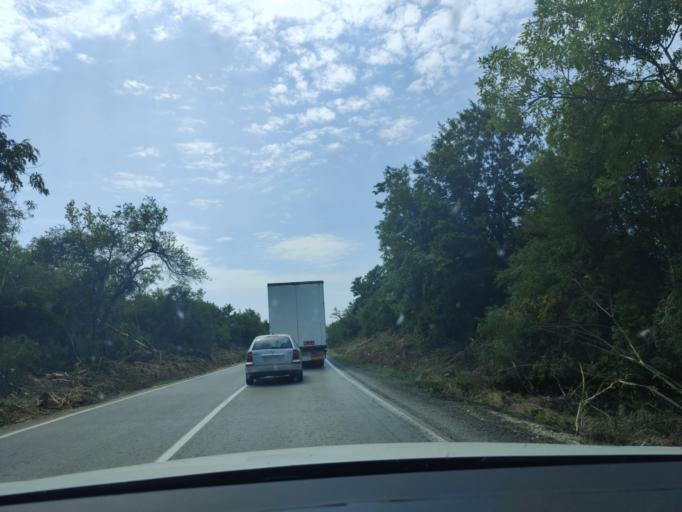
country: BG
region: Vidin
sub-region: Obshtina Ruzhintsi
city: Ruzhintsi
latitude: 43.6747
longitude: 22.7729
